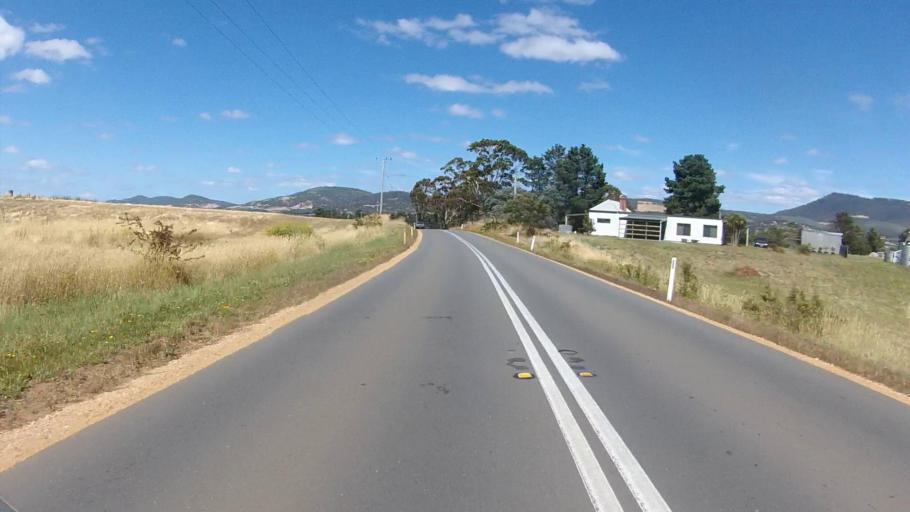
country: AU
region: Tasmania
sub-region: Clarence
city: Cambridge
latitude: -42.7488
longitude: 147.4171
